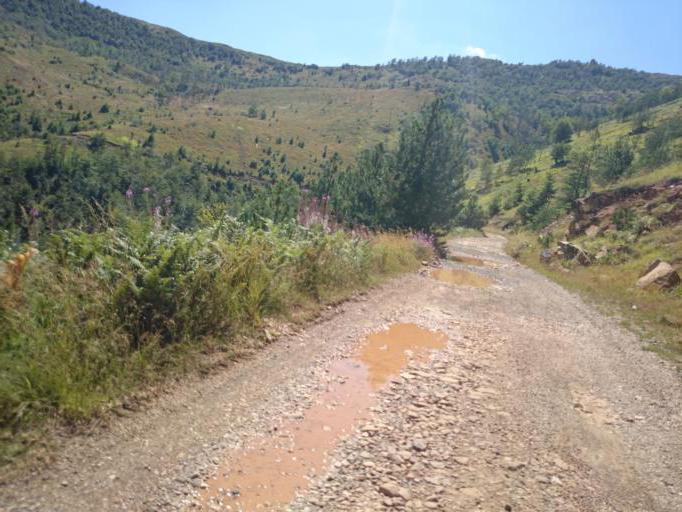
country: AL
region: Diber
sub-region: Rrethi i Bulqizes
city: Zerqan
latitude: 41.4242
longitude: 20.3203
